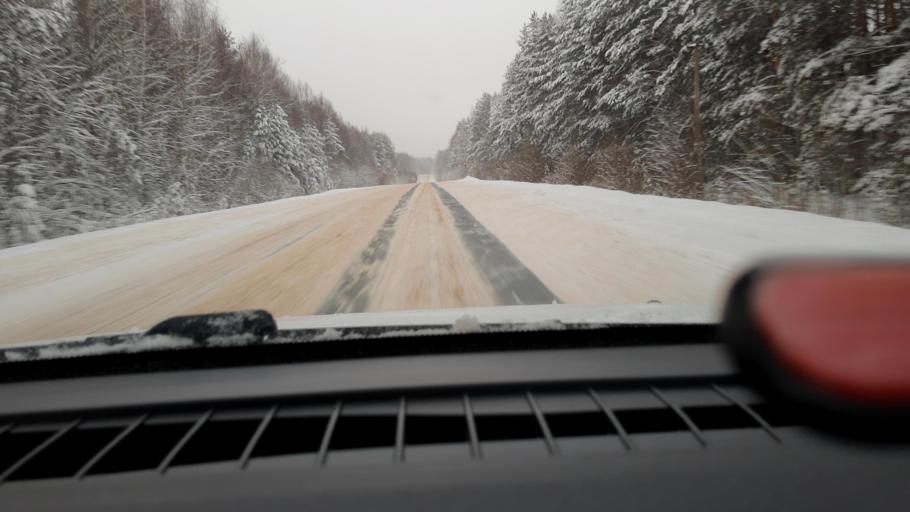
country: RU
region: Nizjnij Novgorod
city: Tonkino
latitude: 57.2904
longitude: 46.4620
